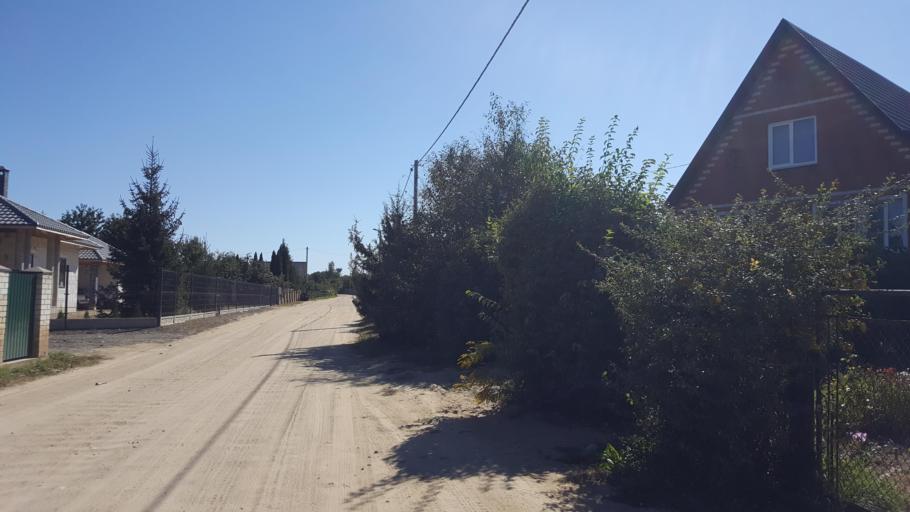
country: BY
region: Brest
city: Vysokaye
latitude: 52.2520
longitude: 23.4957
